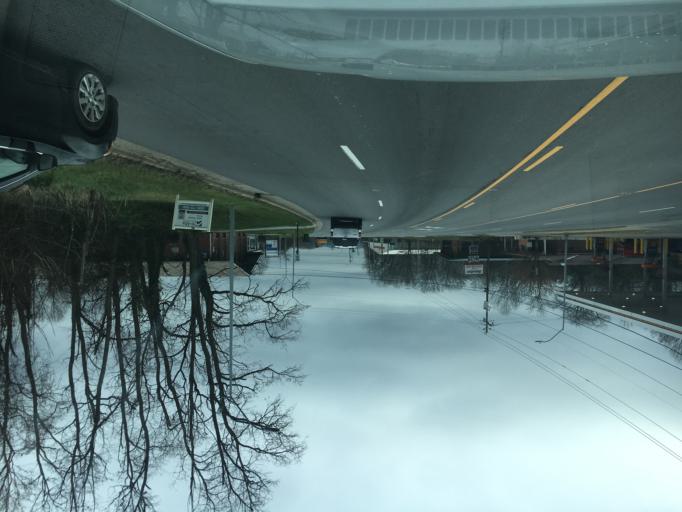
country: US
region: North Carolina
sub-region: Buncombe County
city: Woodfin
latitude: 35.5922
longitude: -82.6058
